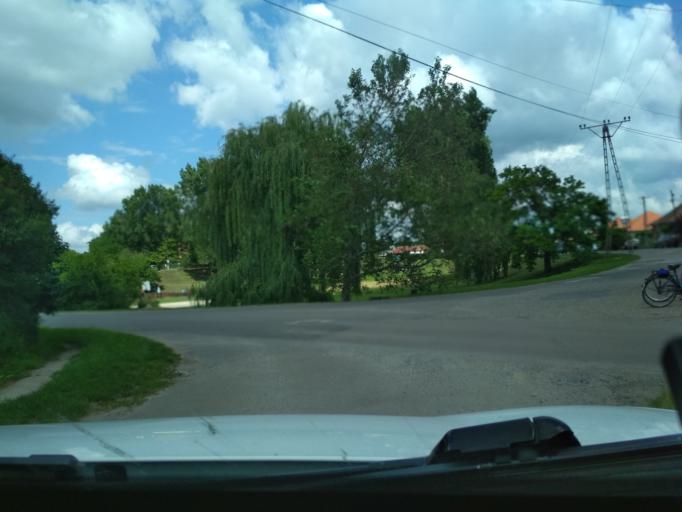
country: HU
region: Jasz-Nagykun-Szolnok
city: Tiszafured
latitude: 47.6092
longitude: 20.7713
